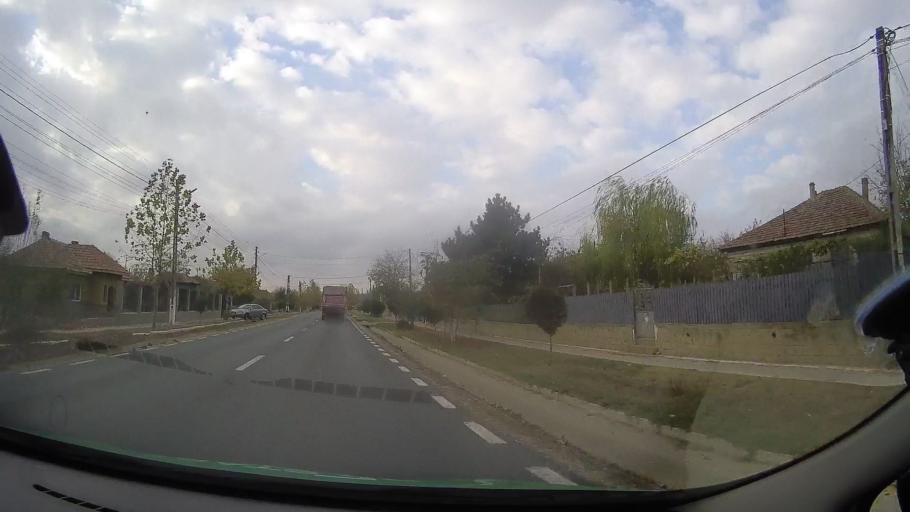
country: RO
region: Constanta
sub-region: Comuna Mircea Voda
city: Satu Nou
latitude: 44.2665
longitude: 28.2294
